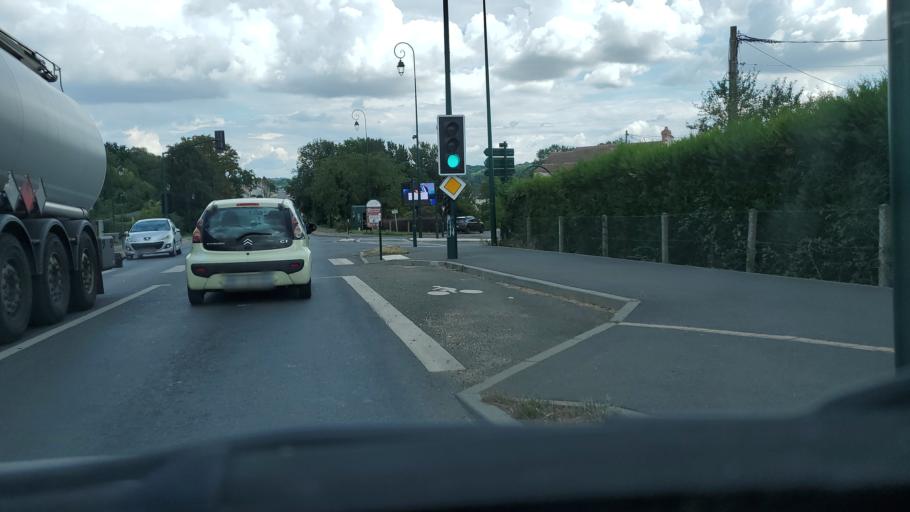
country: FR
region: Ile-de-France
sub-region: Departement de Seine-et-Marne
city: Mouroux
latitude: 48.8240
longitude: 3.0407
